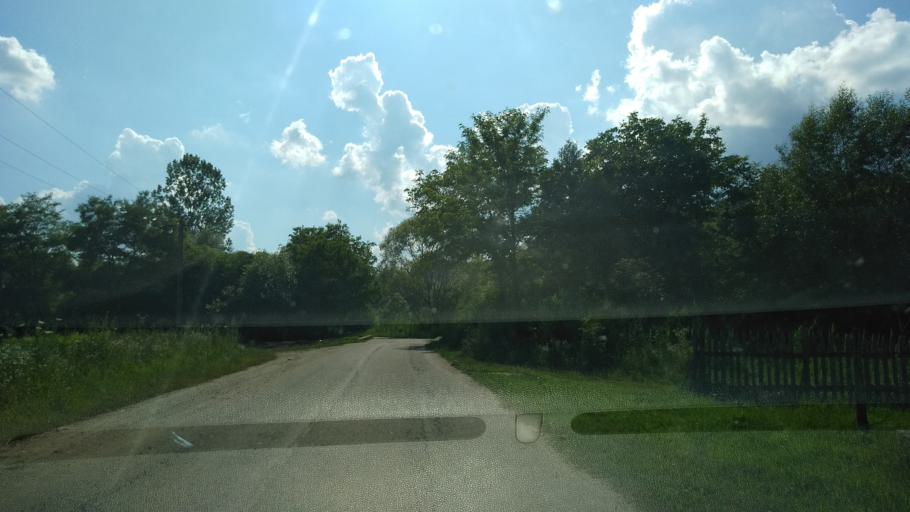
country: RO
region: Hunedoara
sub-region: Comuna Bosorod
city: Bosorod
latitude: 45.7118
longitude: 23.1182
